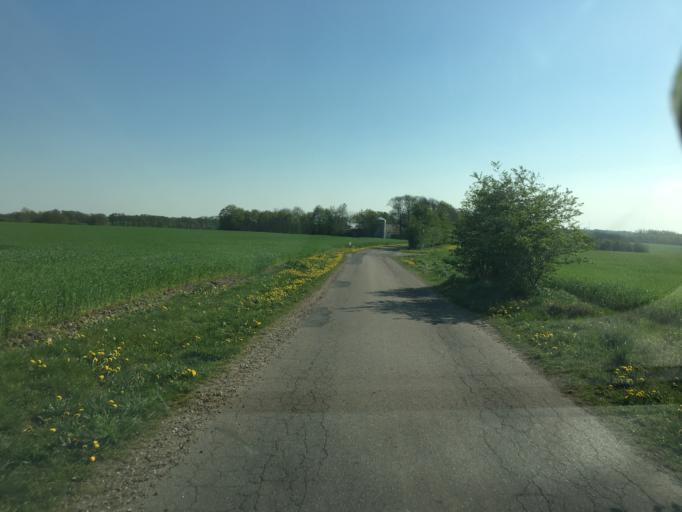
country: DK
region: South Denmark
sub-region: Tonder Kommune
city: Toftlund
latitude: 55.1698
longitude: 9.1012
